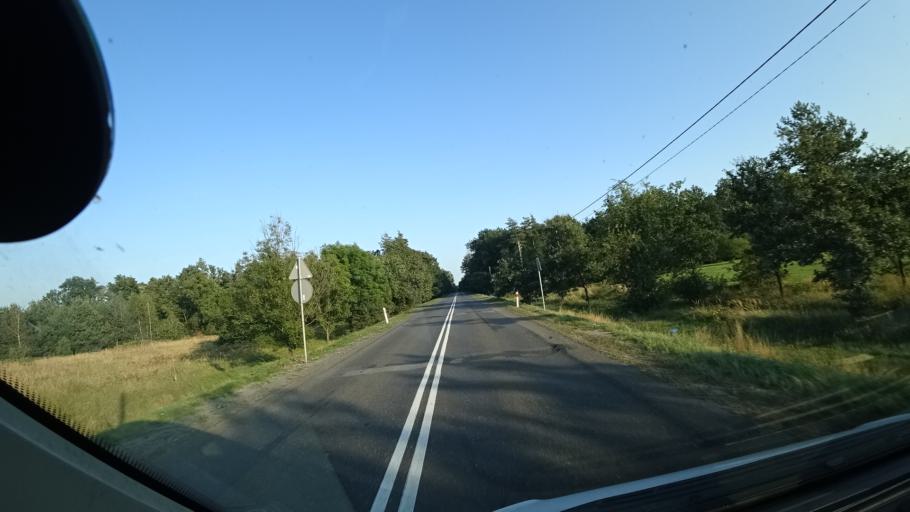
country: PL
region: Opole Voivodeship
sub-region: Powiat kedzierzynsko-kozielski
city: Kedzierzyn-Kozle
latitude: 50.3238
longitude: 18.2134
